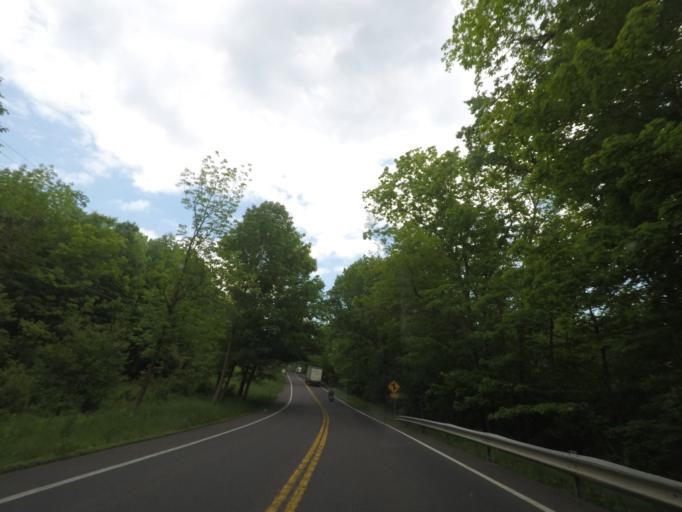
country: US
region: New York
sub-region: Dutchess County
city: Pine Plains
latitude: 42.0548
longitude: -73.6519
